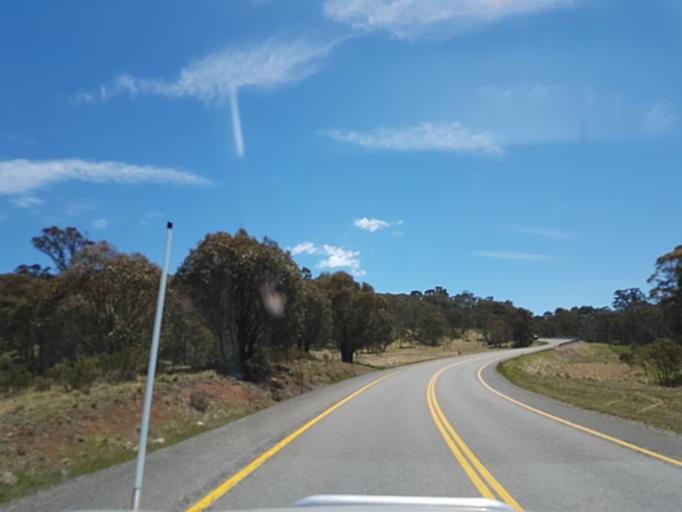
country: AU
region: Victoria
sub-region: Alpine
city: Mount Beauty
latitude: -37.0461
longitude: 147.3137
